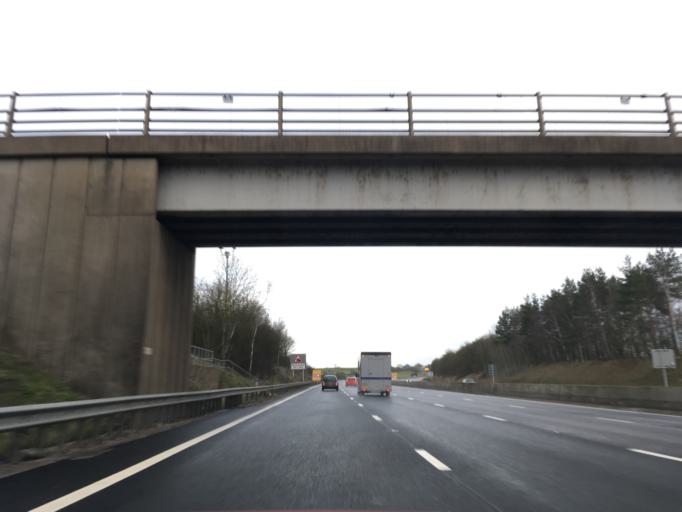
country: GB
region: England
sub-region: Worcestershire
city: Bromsgrove
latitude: 52.3205
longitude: -2.0953
